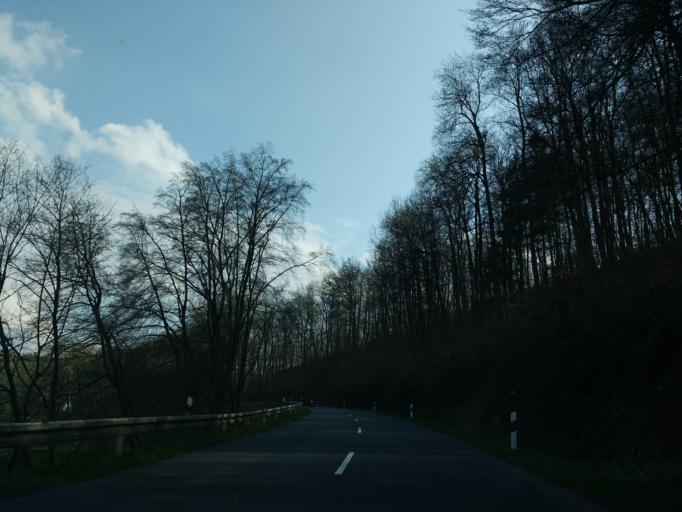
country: DE
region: North Rhine-Westphalia
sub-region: Regierungsbezirk Detmold
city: Paderborn
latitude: 51.6394
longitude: 8.7388
